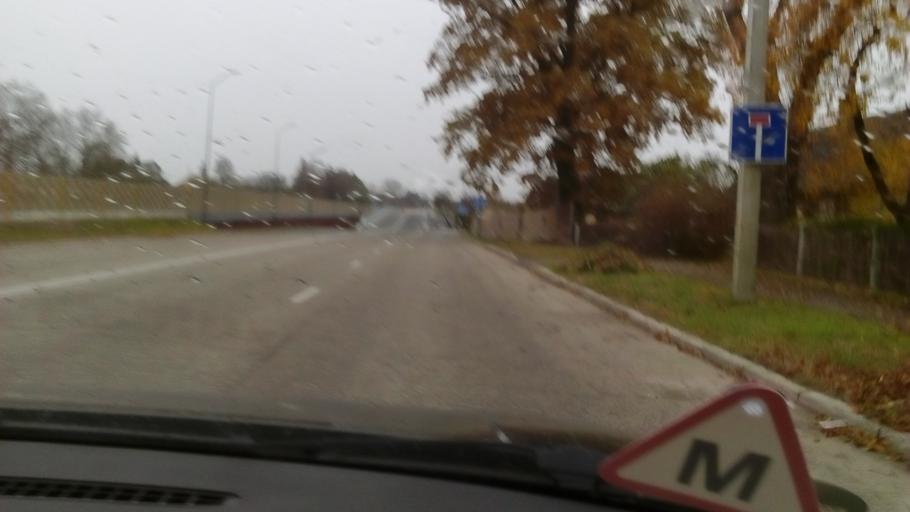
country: LT
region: Marijampoles apskritis
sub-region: Marijampole Municipality
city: Marijampole
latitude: 54.5462
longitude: 23.3568
